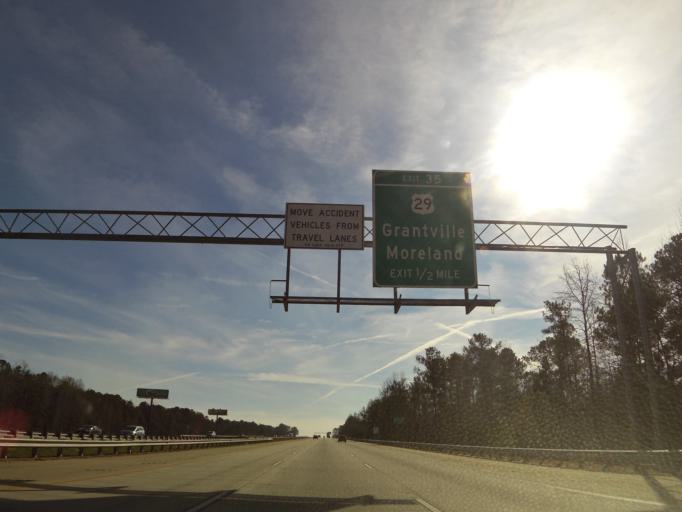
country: US
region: Georgia
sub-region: Coweta County
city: Grantville
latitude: 33.2501
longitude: -84.8063
